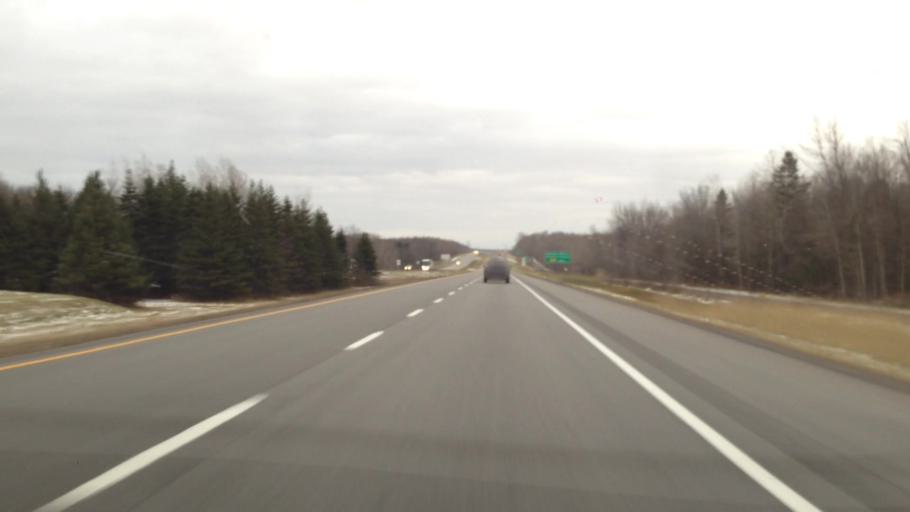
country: CA
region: Quebec
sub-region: Monteregie
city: Rigaud
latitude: 45.5322
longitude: -74.3810
